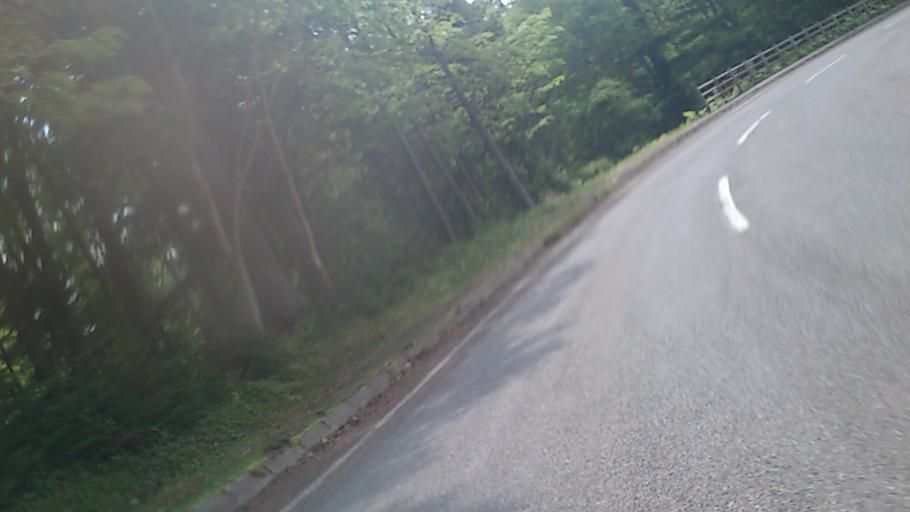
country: JP
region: Hokkaido
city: Kitami
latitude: 43.3906
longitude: 143.9702
